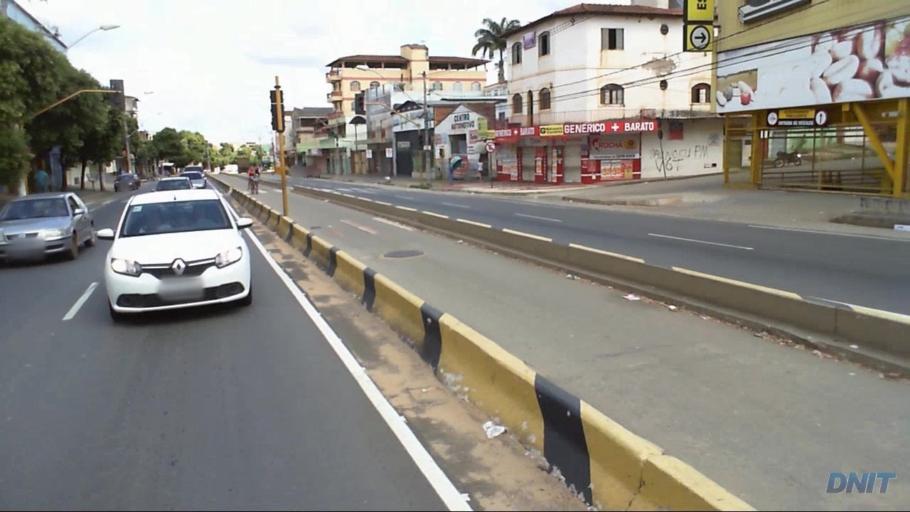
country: BR
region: Minas Gerais
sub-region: Governador Valadares
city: Governador Valadares
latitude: -18.8787
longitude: -41.9621
